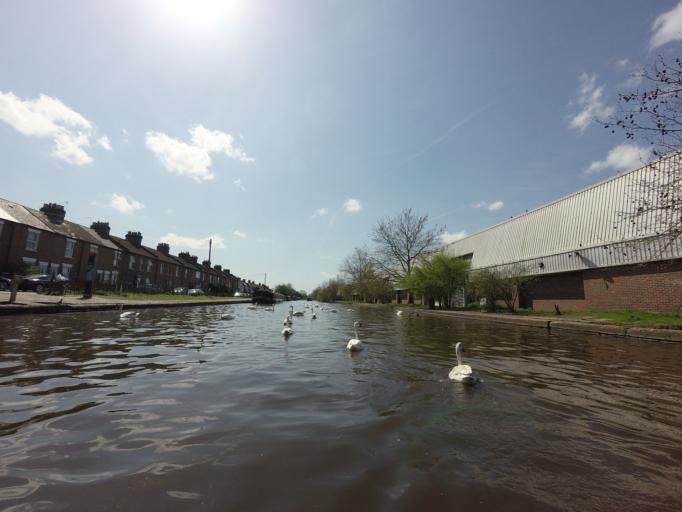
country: GB
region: England
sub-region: Greater London
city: Southall
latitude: 51.5128
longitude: -0.3906
